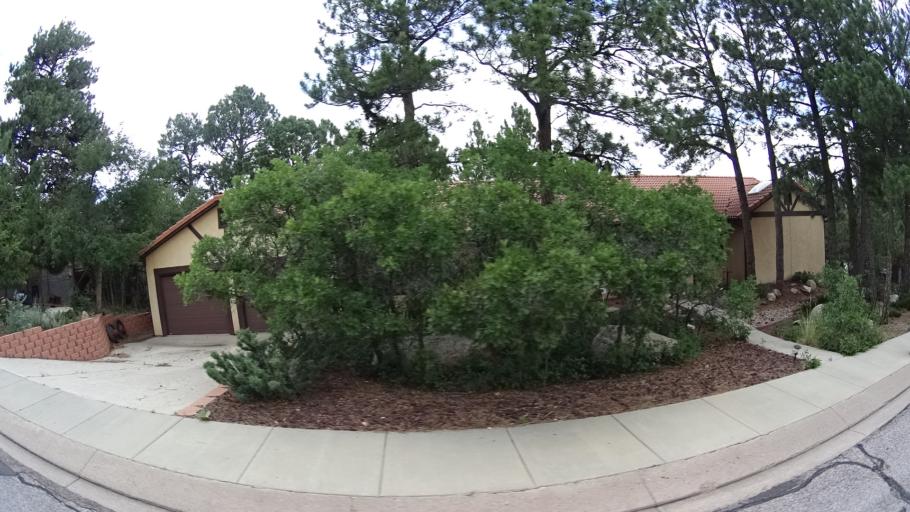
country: US
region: Colorado
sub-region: El Paso County
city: Colorado Springs
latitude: 38.9076
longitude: -104.8482
